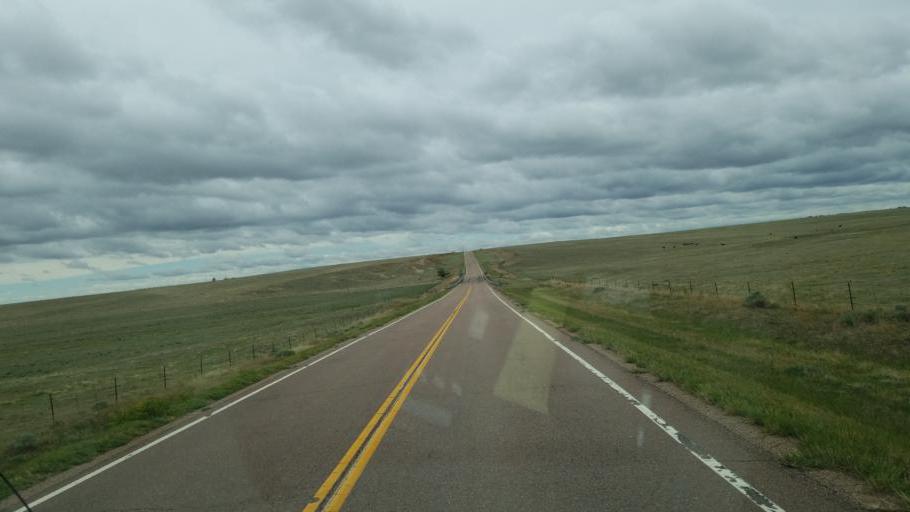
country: US
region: Colorado
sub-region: Lincoln County
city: Limon
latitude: 38.8392
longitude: -103.9026
